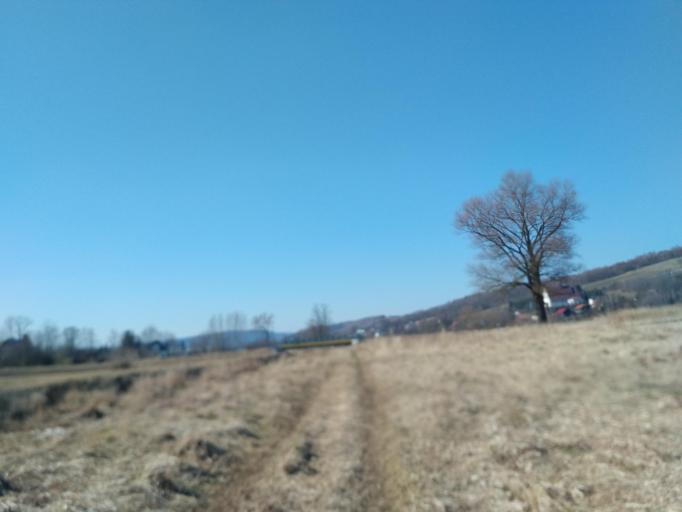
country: PL
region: Subcarpathian Voivodeship
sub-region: Powiat brzozowski
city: Domaradz
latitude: 49.8008
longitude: 21.9097
